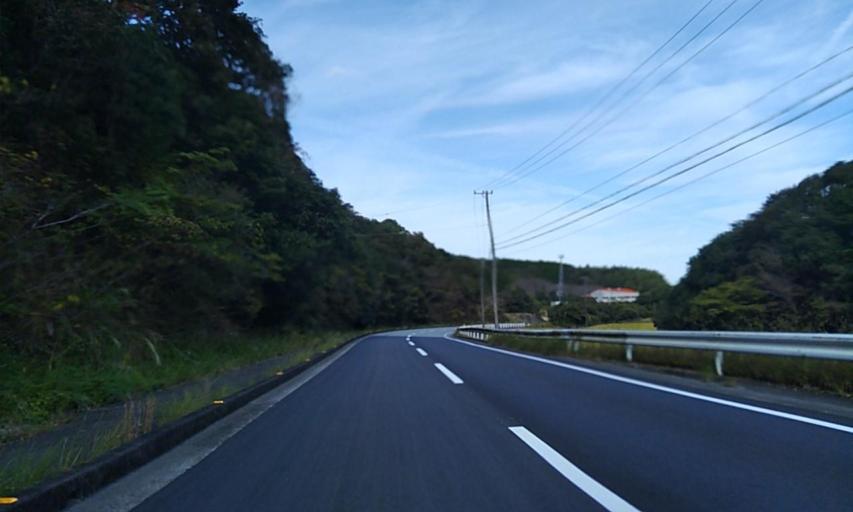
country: JP
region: Mie
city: Ise
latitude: 34.3564
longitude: 136.7539
